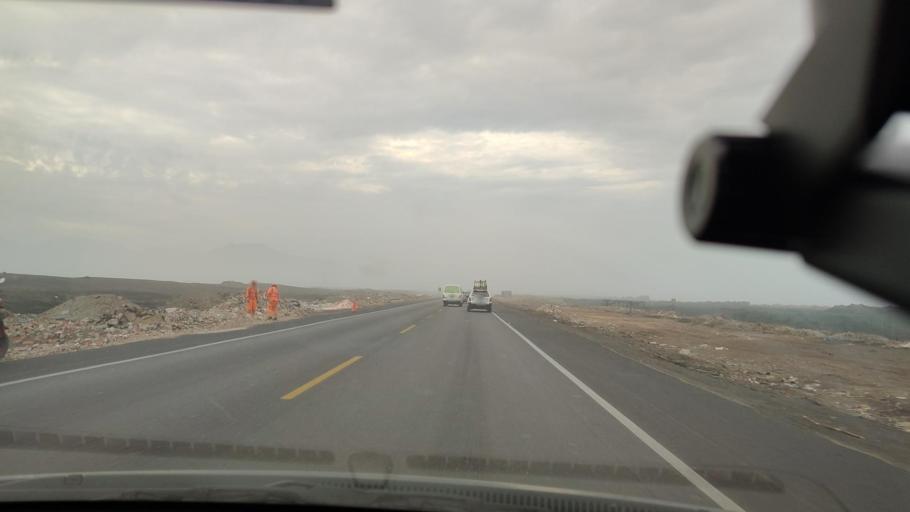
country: PE
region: La Libertad
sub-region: Provincia de Trujillo
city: Buenos Aires
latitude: -8.1197
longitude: -79.0847
